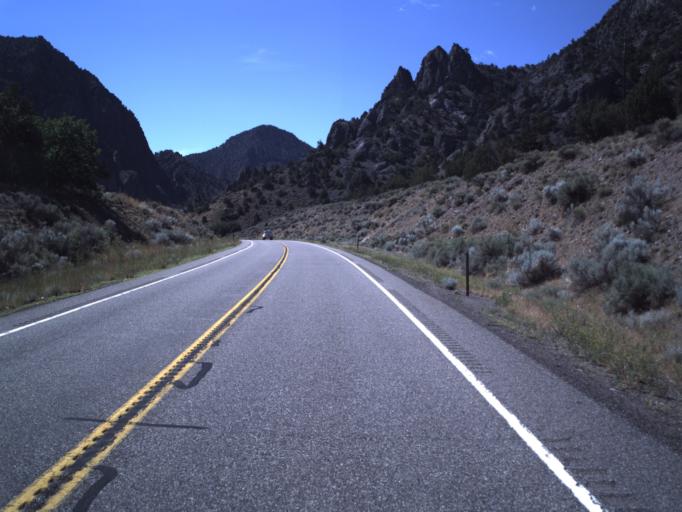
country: US
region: Utah
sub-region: Sevier County
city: Monroe
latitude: 38.5558
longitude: -112.2717
